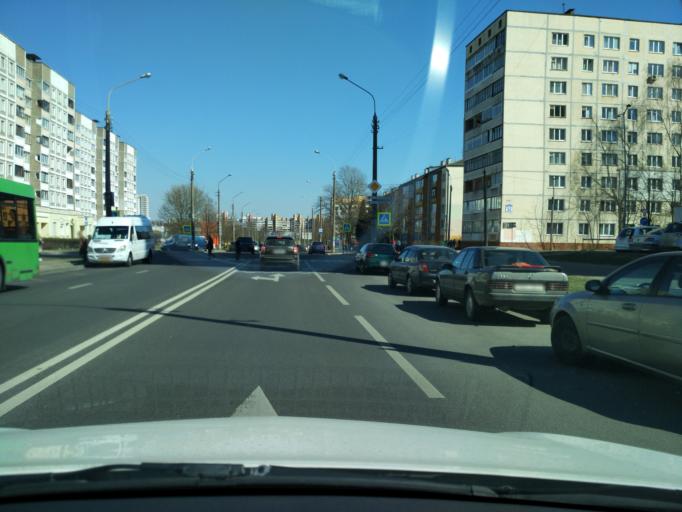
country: BY
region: Minsk
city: Minsk
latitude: 53.8774
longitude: 27.5553
